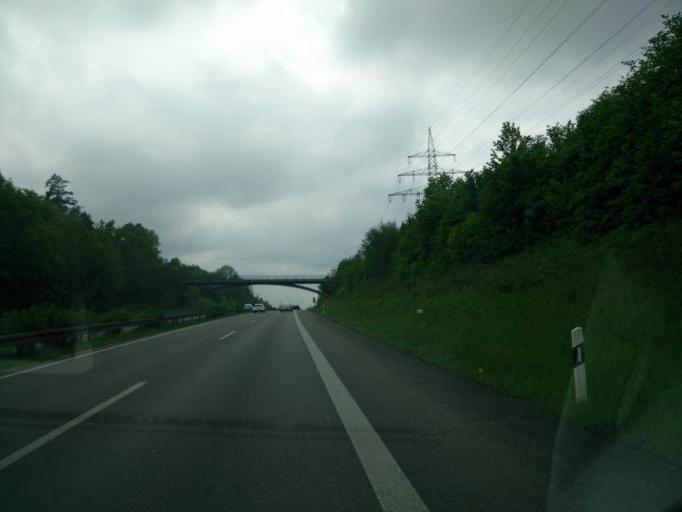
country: DE
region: Baden-Wuerttemberg
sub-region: Tuebingen Region
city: Eningen unter Achalm
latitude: 48.5115
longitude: 9.2411
